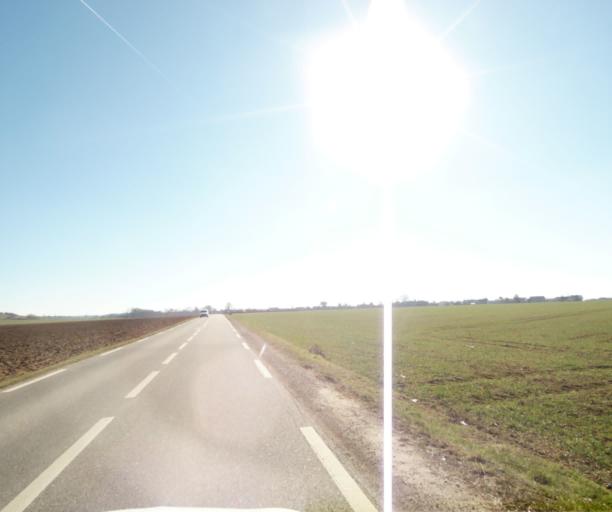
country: FR
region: Lorraine
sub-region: Departement de Meurthe-et-Moselle
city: Saulxures-les-Nancy
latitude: 48.6975
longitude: 6.2491
